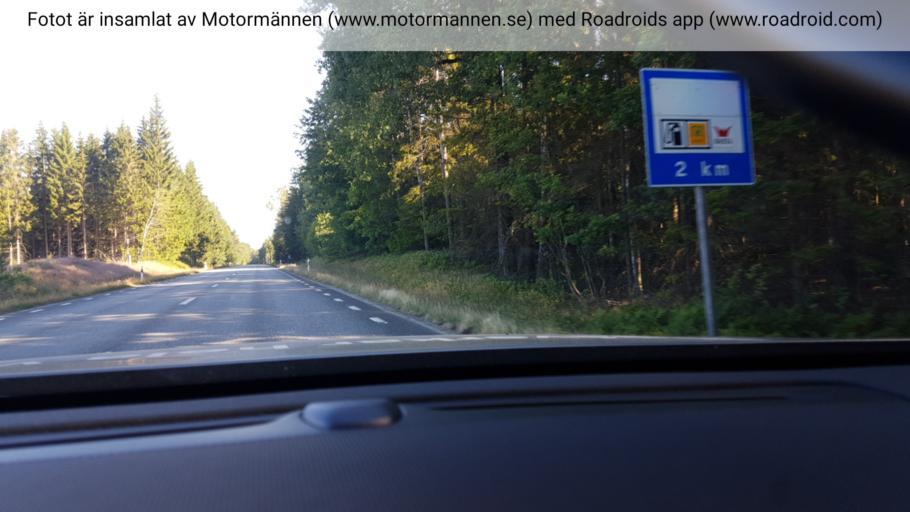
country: SE
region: Kronoberg
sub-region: Markaryds Kommun
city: Markaryd
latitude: 56.4286
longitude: 13.6214
